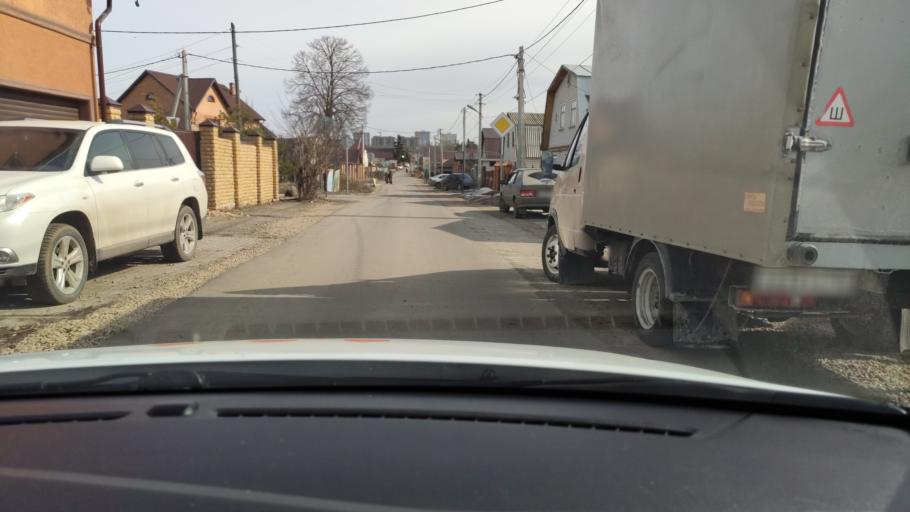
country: RU
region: Tatarstan
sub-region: Gorod Kazan'
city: Kazan
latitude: 55.7254
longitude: 49.1412
